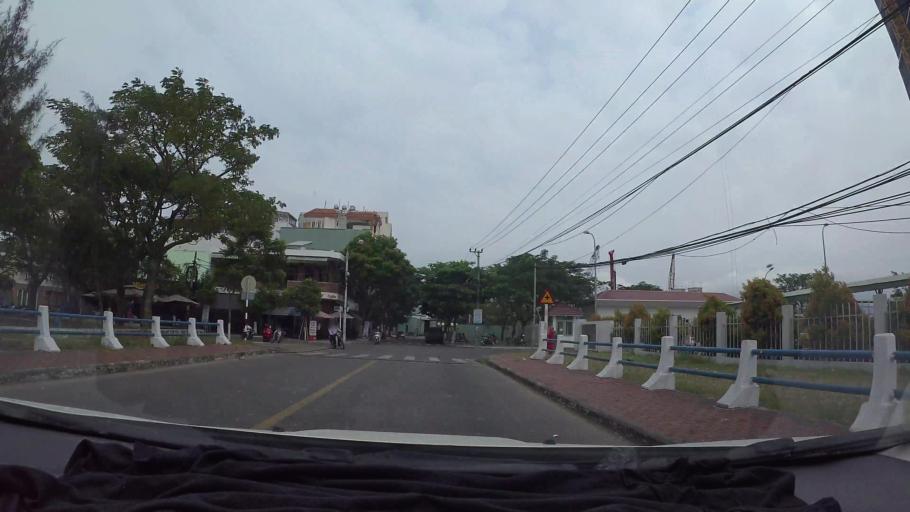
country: VN
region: Da Nang
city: Da Nang
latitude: 16.0867
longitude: 108.2200
